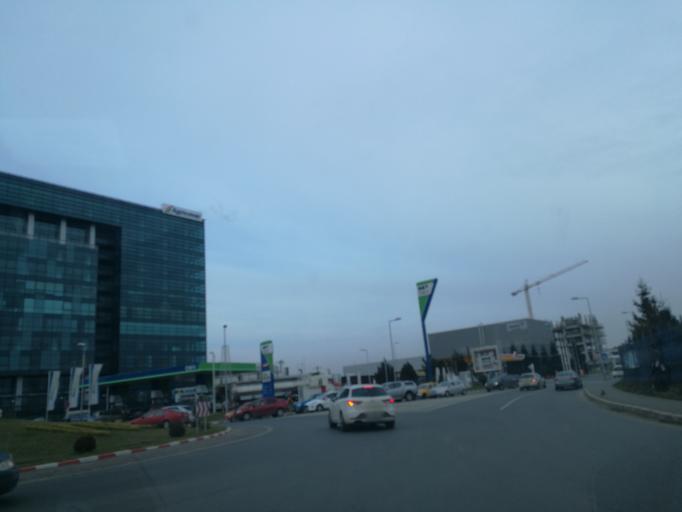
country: RO
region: Ilfov
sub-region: Voluntari City
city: Voluntari
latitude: 44.4924
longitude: 26.1267
